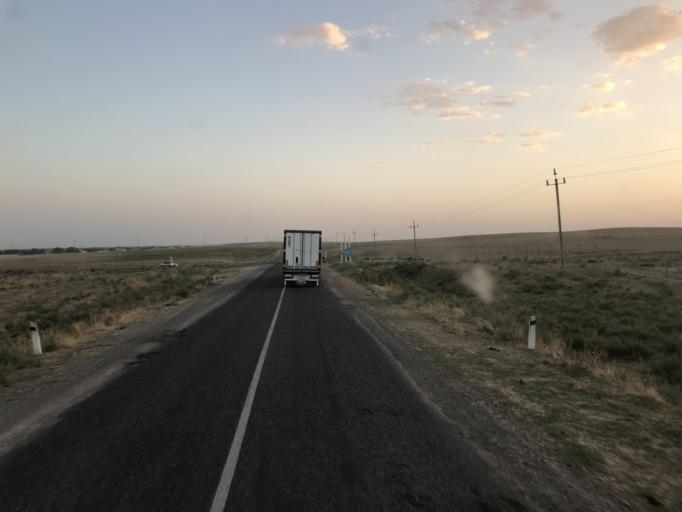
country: UZ
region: Toshkent
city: Amir Timur
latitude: 41.3503
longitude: 68.7103
